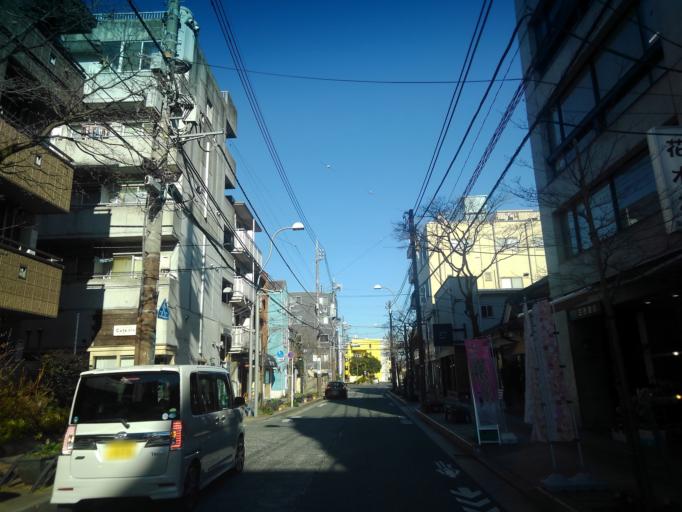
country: JP
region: Tokyo
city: Hachioji
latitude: 35.6614
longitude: 139.3337
